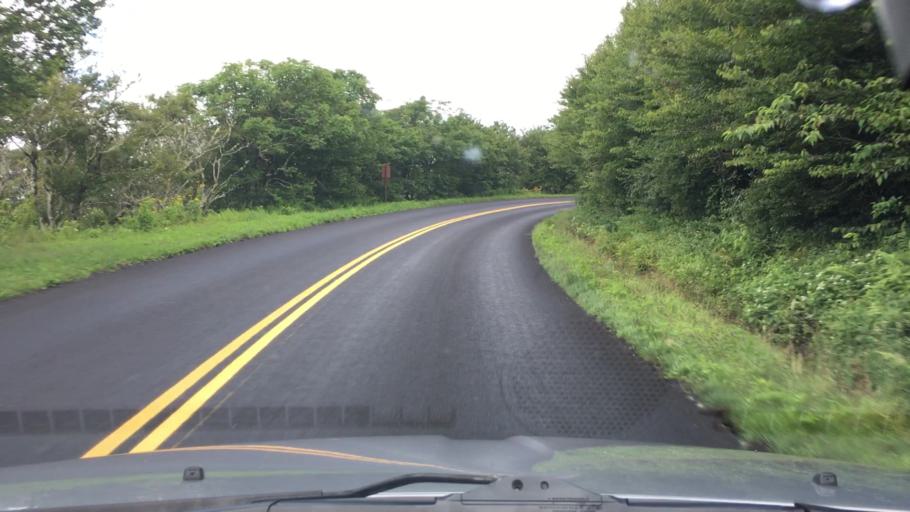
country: US
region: North Carolina
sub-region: Buncombe County
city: Black Mountain
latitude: 35.7122
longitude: -82.3641
